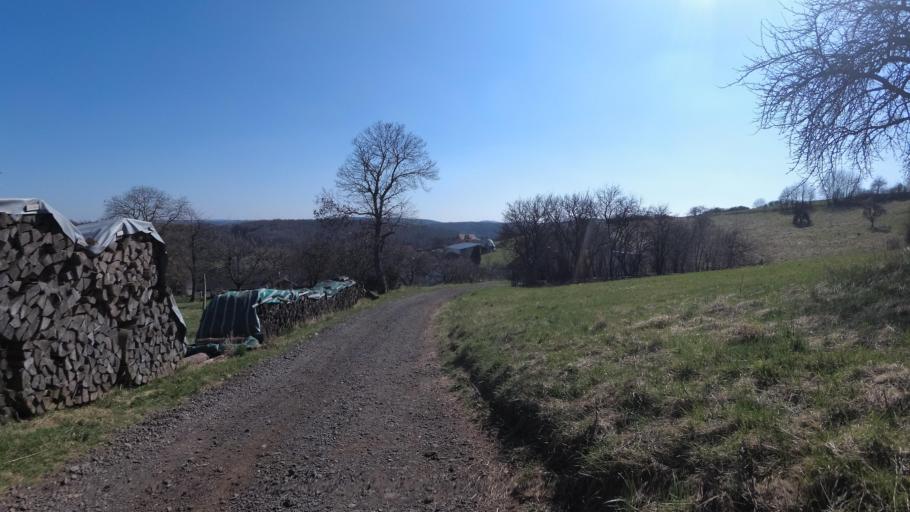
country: DE
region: Rheinland-Pfalz
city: Dambach
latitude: 49.6288
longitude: 7.1302
